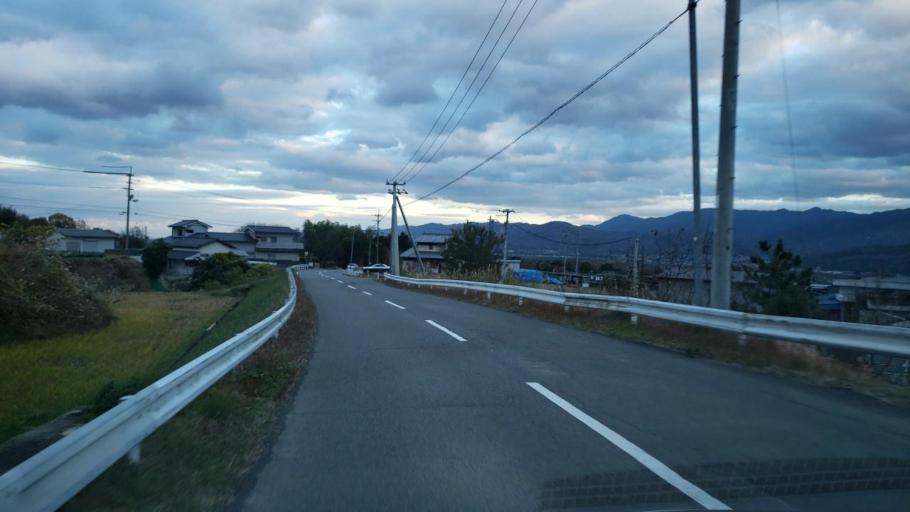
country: JP
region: Tokushima
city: Wakimachi
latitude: 34.0843
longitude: 134.1862
